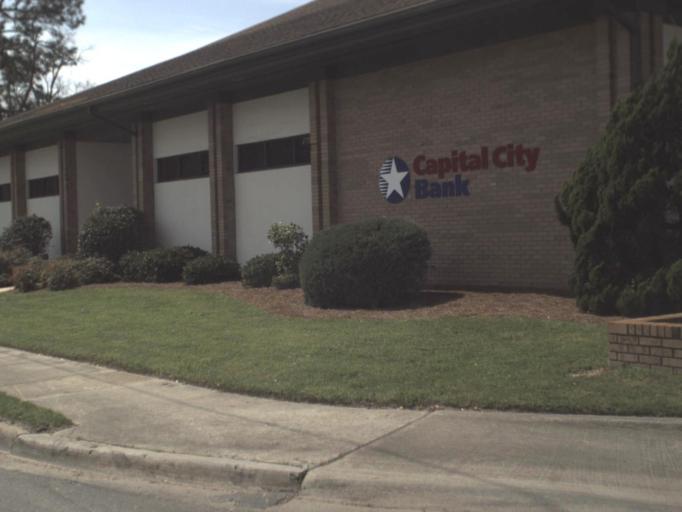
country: US
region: Florida
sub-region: Gadsden County
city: Havana
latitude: 30.6239
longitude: -84.4154
